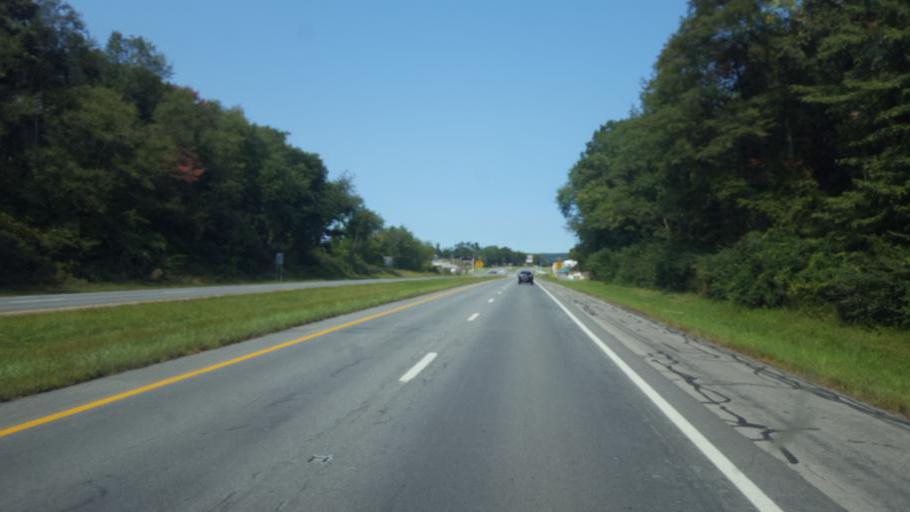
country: US
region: Ohio
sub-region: Wayne County
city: Wooster
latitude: 40.7759
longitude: -81.9704
